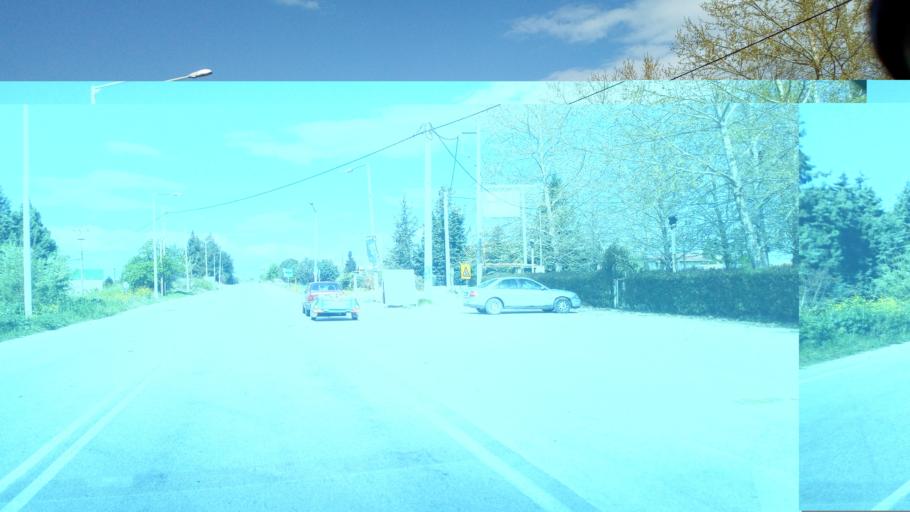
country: GR
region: Central Macedonia
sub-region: Nomos Kilkis
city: Nea Santa
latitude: 40.8333
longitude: 22.9157
